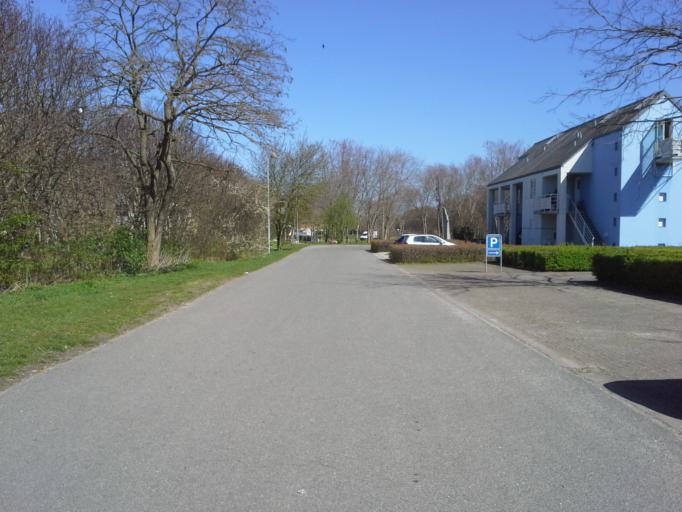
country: DK
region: South Denmark
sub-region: Odense Kommune
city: Neder Holluf
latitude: 55.3799
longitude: 10.4509
